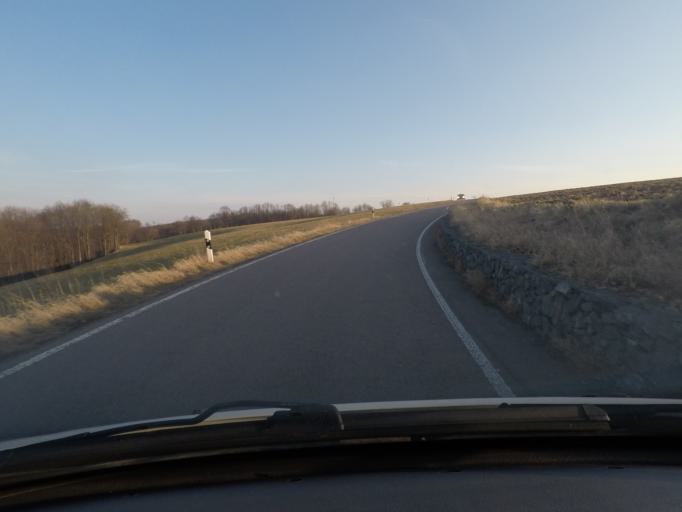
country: DE
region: Saxony
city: Reinhardtsgrimma
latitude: 50.9174
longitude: 13.7963
